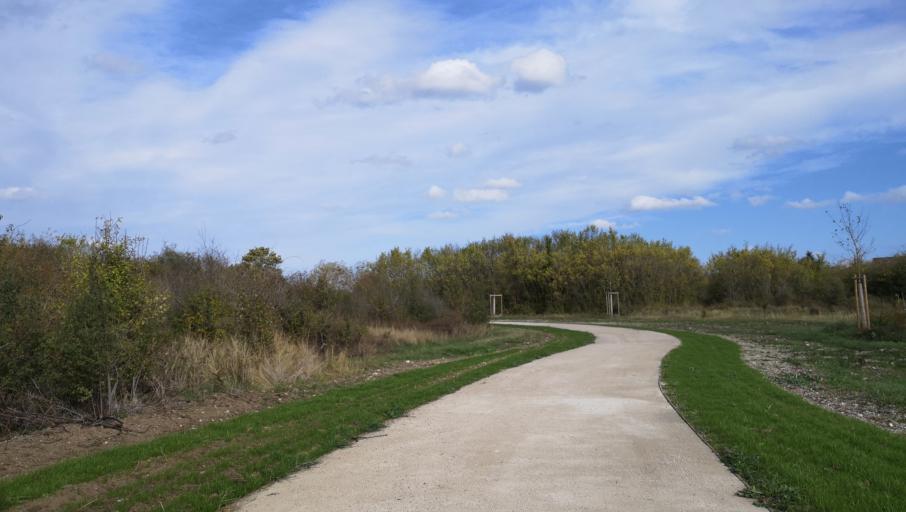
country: FR
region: Centre
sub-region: Departement du Loiret
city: Orleans
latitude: 47.9182
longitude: 1.8869
